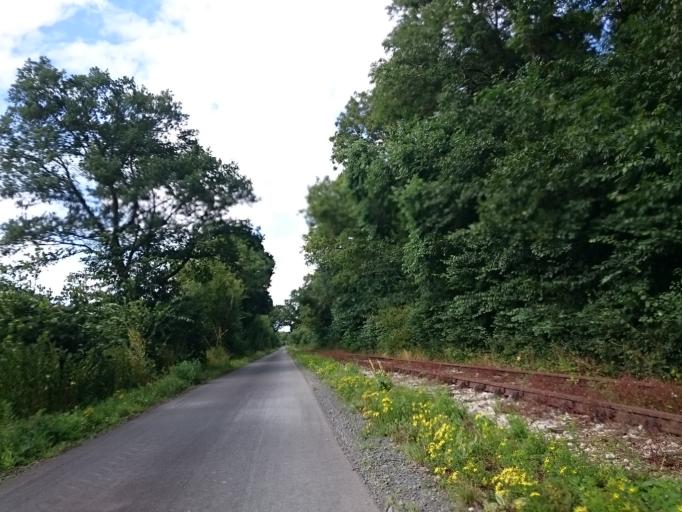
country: FR
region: Lower Normandy
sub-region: Departement du Calvados
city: Sainte-Honorine-du-Fay
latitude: 49.0382
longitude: -0.4646
